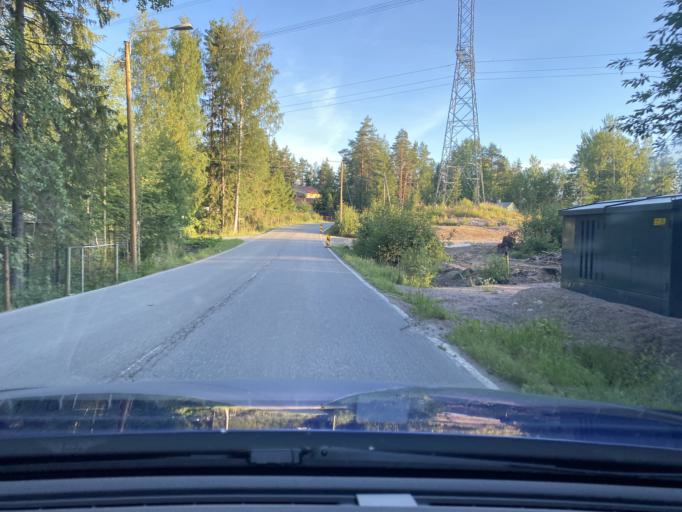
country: FI
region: Uusimaa
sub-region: Helsinki
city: Nurmijaervi
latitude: 60.4068
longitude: 24.7652
